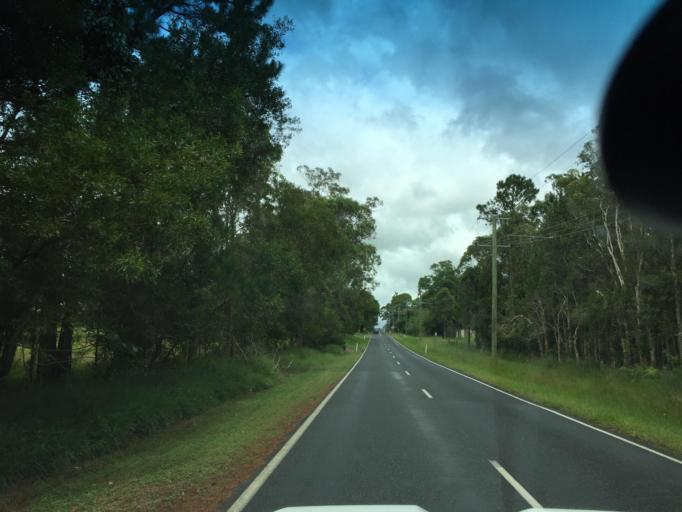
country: AU
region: Queensland
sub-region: Moreton Bay
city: Caboolture
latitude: -27.0537
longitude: 152.9112
